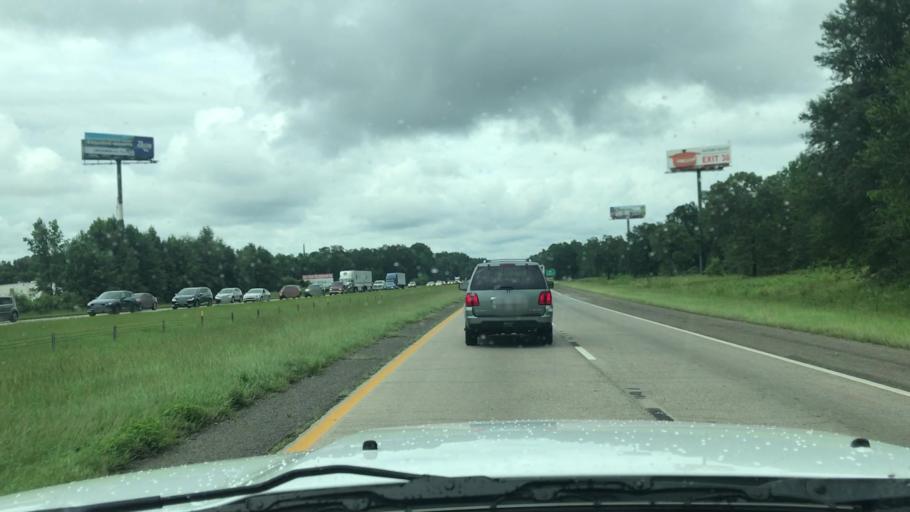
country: US
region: South Carolina
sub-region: Hampton County
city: Yemassee
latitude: 32.6961
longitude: -80.8771
